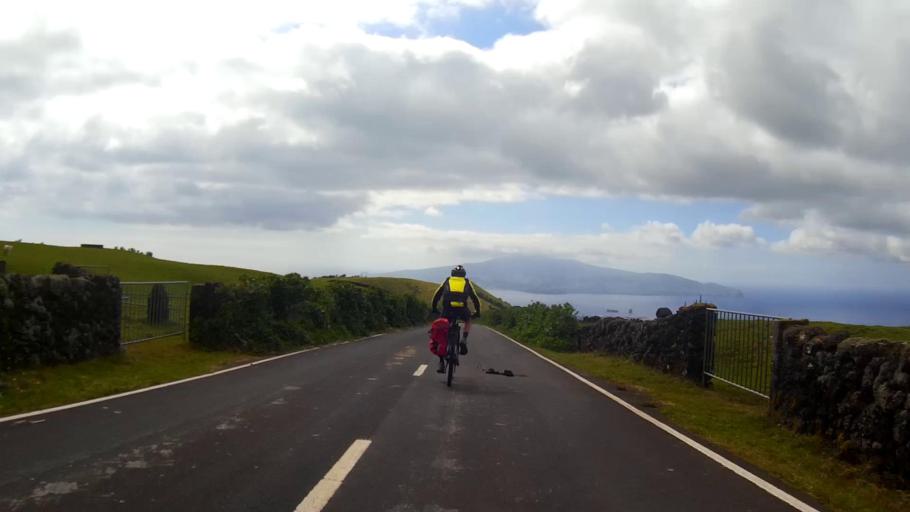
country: PT
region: Azores
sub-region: Madalena
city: Madalena
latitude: 38.4958
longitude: -28.4567
